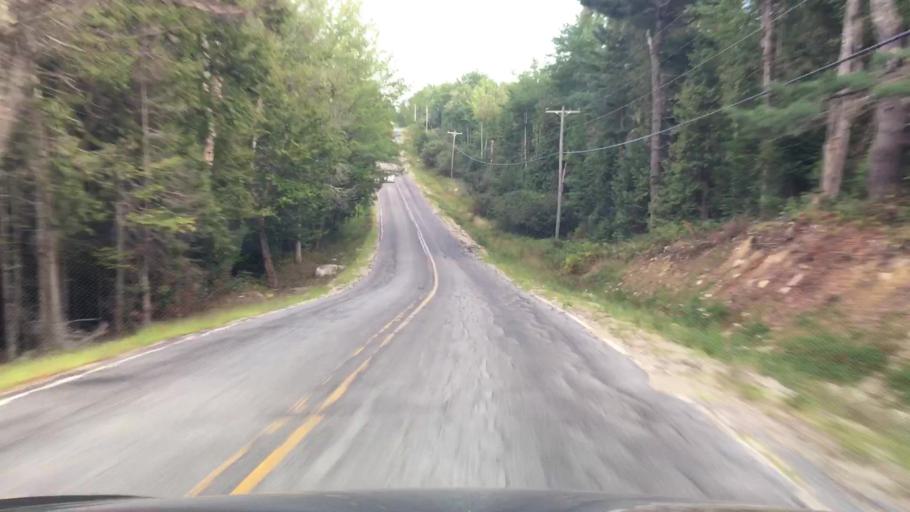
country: US
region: Maine
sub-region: Hancock County
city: Surry
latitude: 44.5064
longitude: -68.5938
